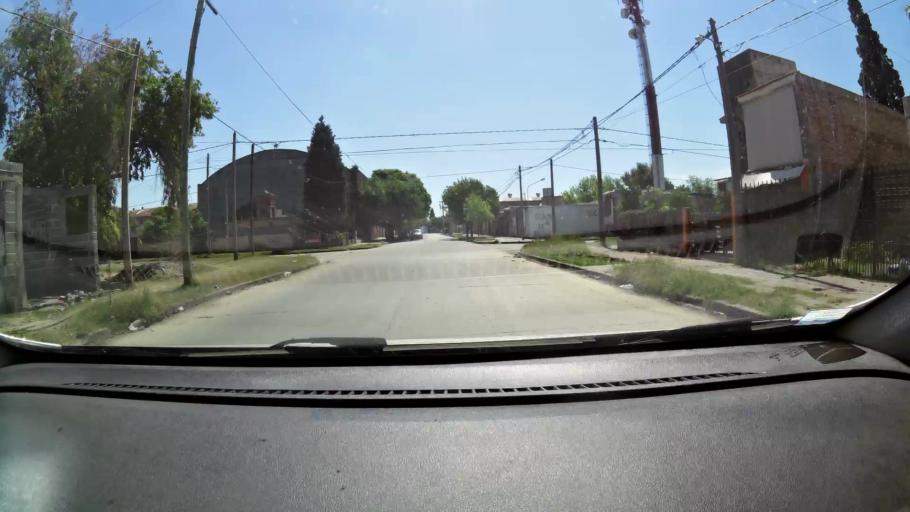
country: AR
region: Cordoba
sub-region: Departamento de Capital
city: Cordoba
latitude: -31.3756
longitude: -64.1461
